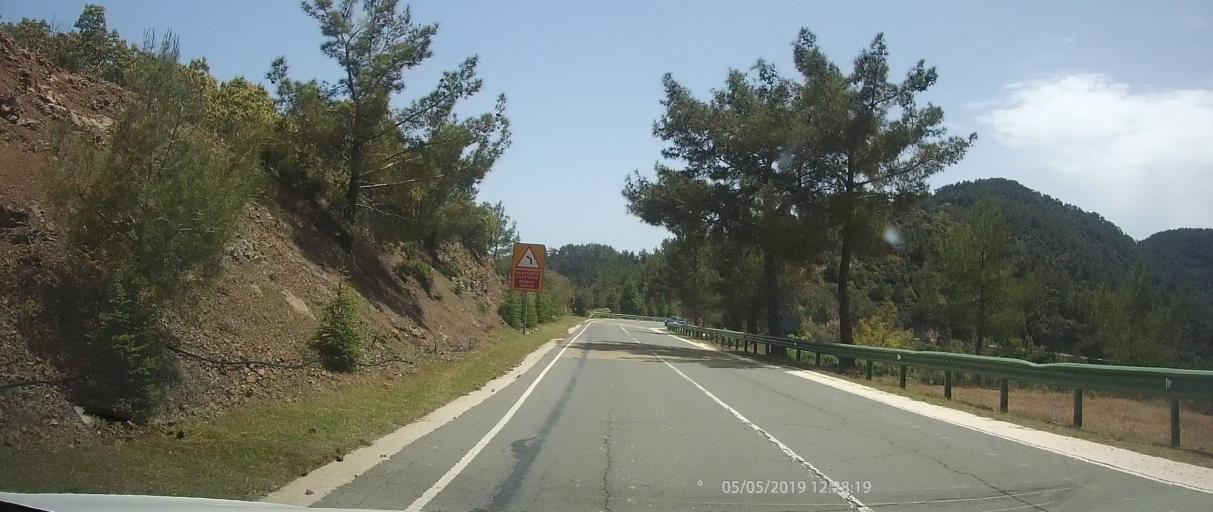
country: CY
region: Lefkosia
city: Kakopetria
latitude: 34.9793
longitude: 32.7424
